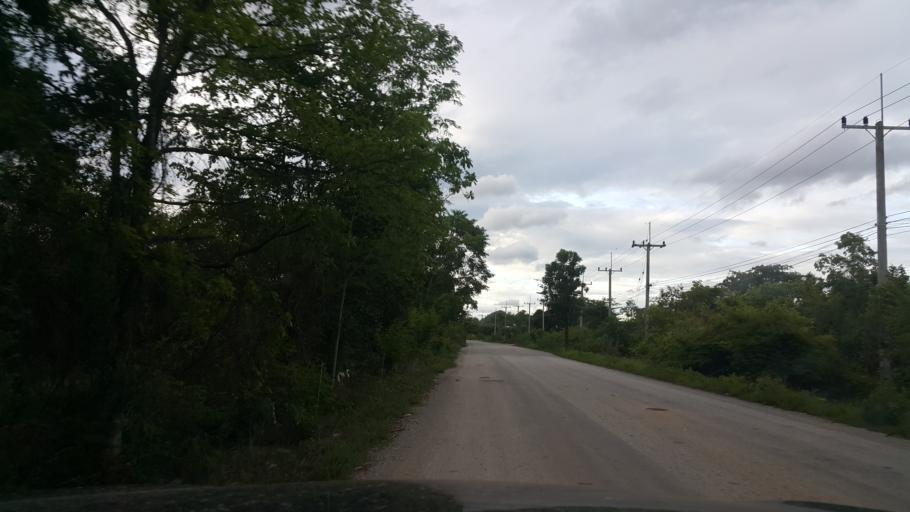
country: TH
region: Sukhothai
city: Thung Saliam
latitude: 17.1756
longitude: 99.5249
